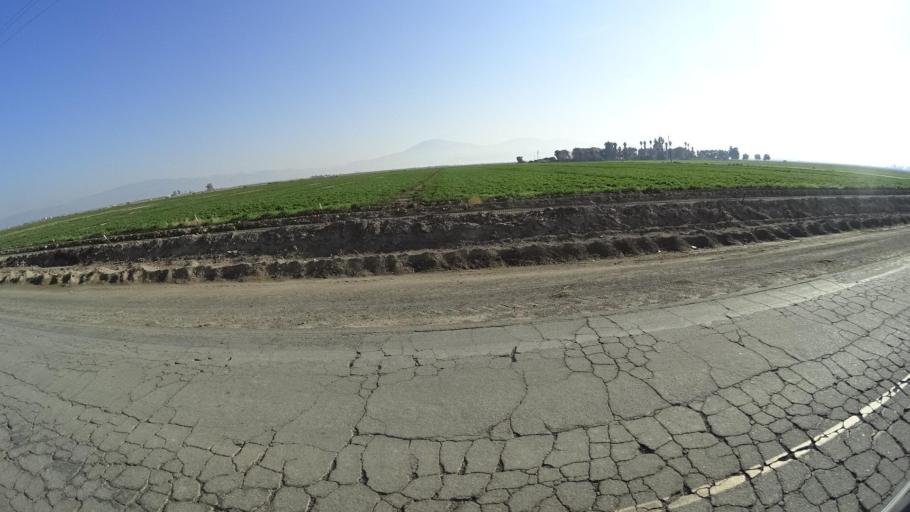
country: US
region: California
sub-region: Kern County
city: Weedpatch
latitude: 35.2022
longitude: -118.9689
